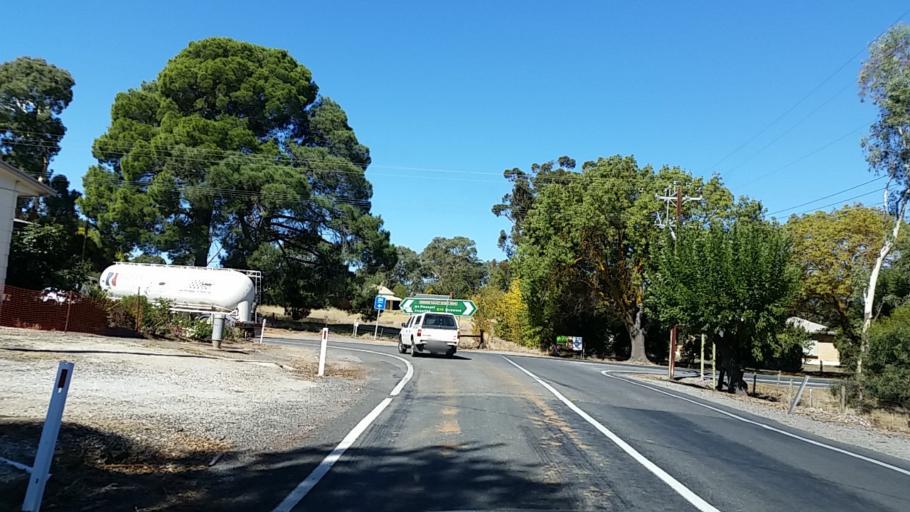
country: AU
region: South Australia
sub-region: Adelaide Hills
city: Birdwood
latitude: -34.7802
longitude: 139.0364
